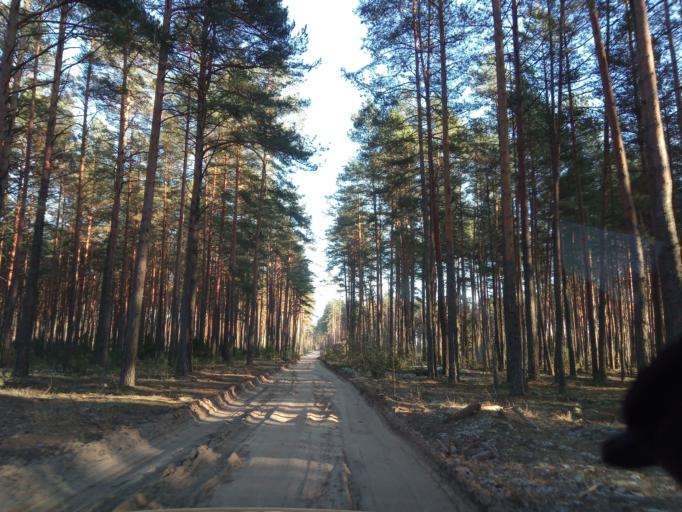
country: LT
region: Alytaus apskritis
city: Druskininkai
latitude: 53.9566
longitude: 23.8734
